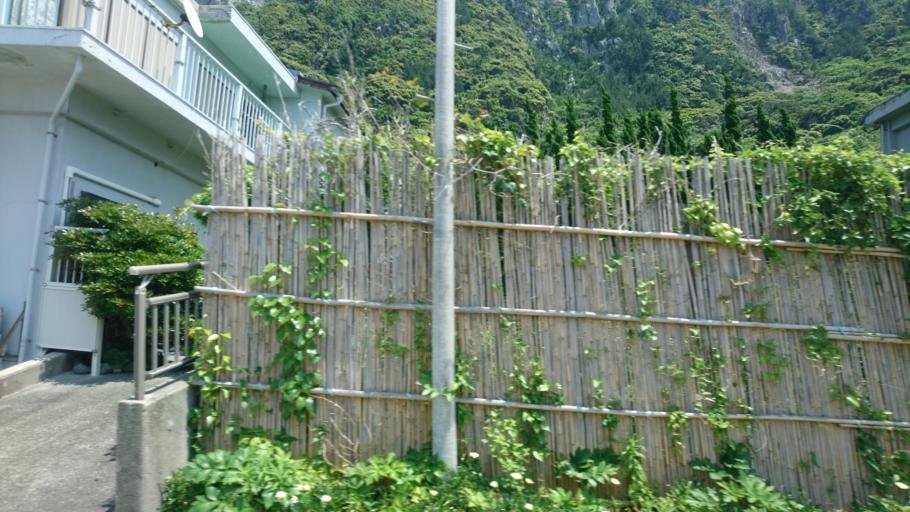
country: JP
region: Shizuoka
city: Shimoda
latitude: 34.4194
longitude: 139.2816
